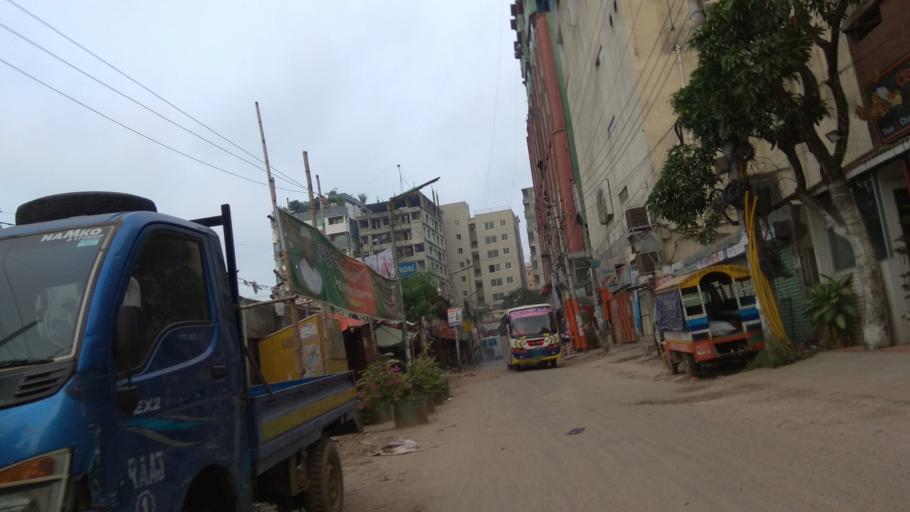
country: BD
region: Dhaka
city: Tungi
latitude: 23.8240
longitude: 90.3653
